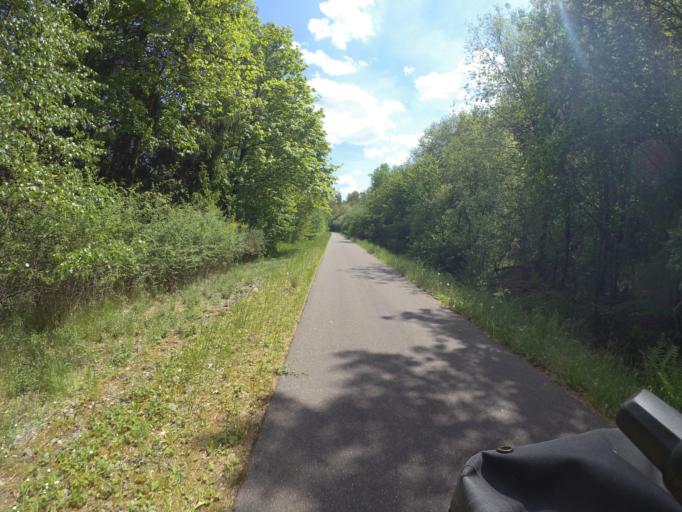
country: DE
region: Rheinland-Pfalz
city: Ormont
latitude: 50.3589
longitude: 6.4645
